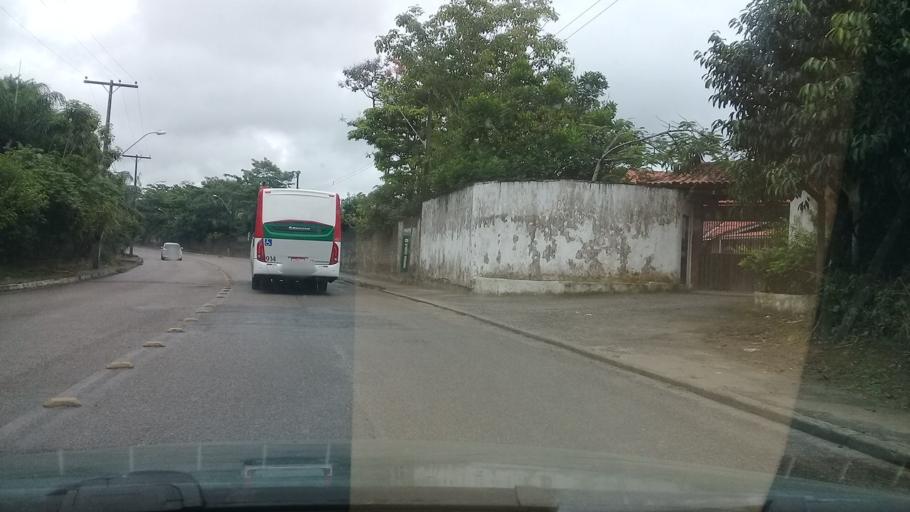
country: BR
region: Pernambuco
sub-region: Jaboatao Dos Guararapes
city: Jaboatao dos Guararapes
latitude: -8.0635
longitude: -34.9859
